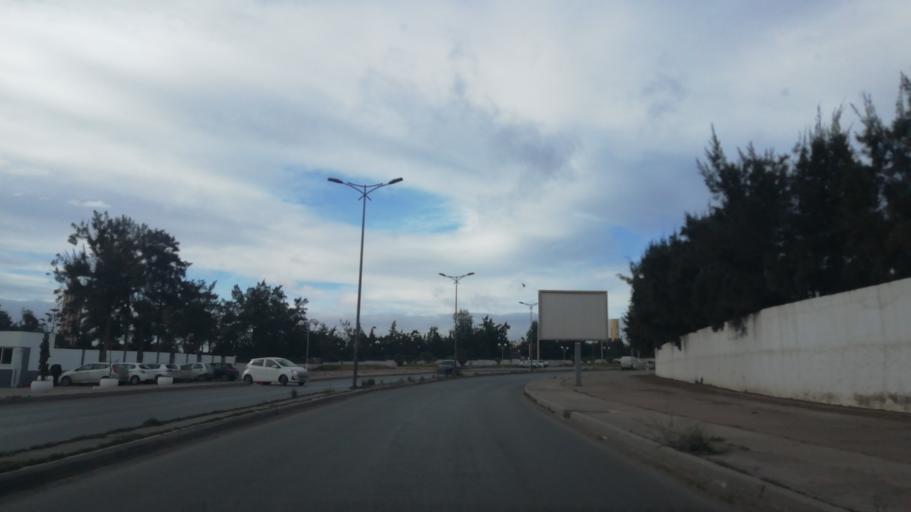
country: DZ
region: Oran
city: Bir el Djir
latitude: 35.7134
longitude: -0.5823
